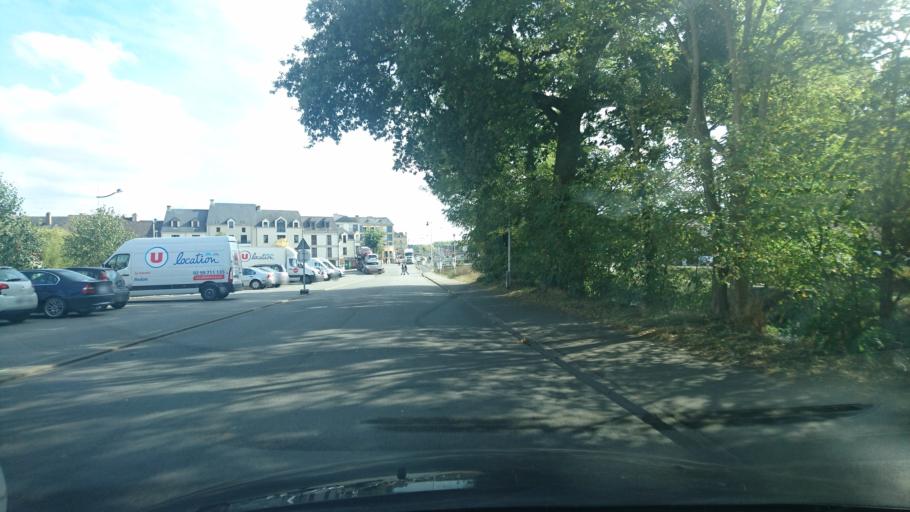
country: FR
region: Brittany
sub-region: Departement d'Ille-et-Vilaine
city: Redon
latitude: 47.6497
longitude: -2.0890
